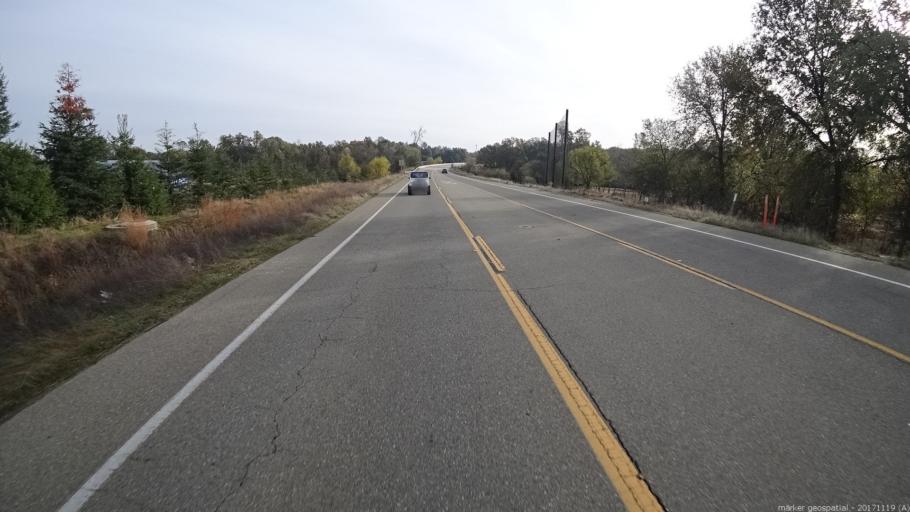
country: US
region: California
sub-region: Shasta County
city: Anderson
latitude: 40.5085
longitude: -122.3190
